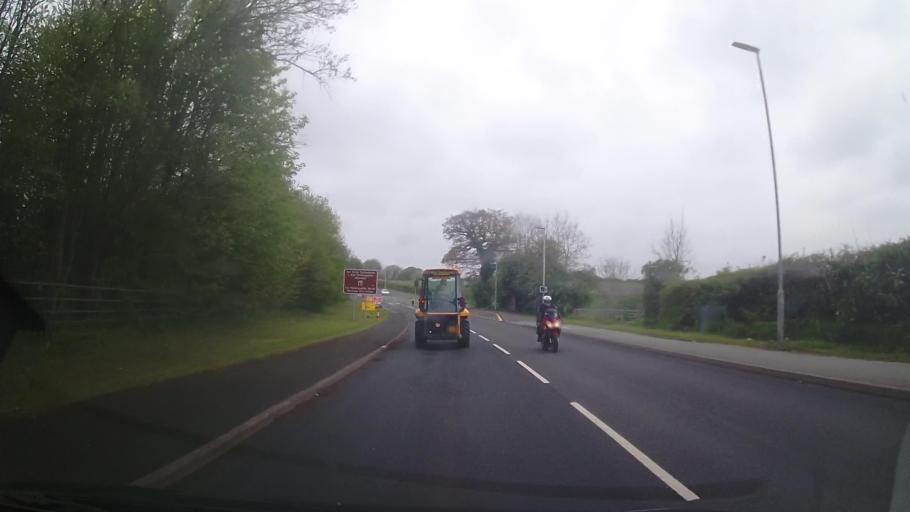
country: GB
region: Wales
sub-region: Wrexham
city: Ruabon
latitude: 52.9852
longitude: -3.0554
